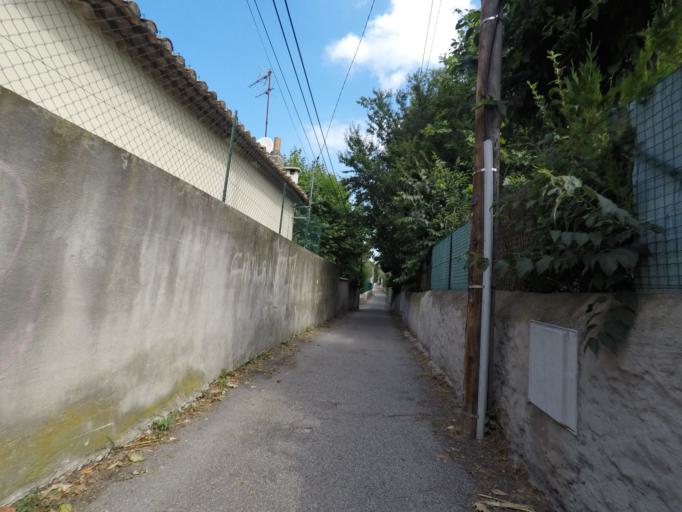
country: FR
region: Provence-Alpes-Cote d'Azur
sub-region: Departement des Bouches-du-Rhone
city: Marseille 09
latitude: 43.2615
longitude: 5.4229
